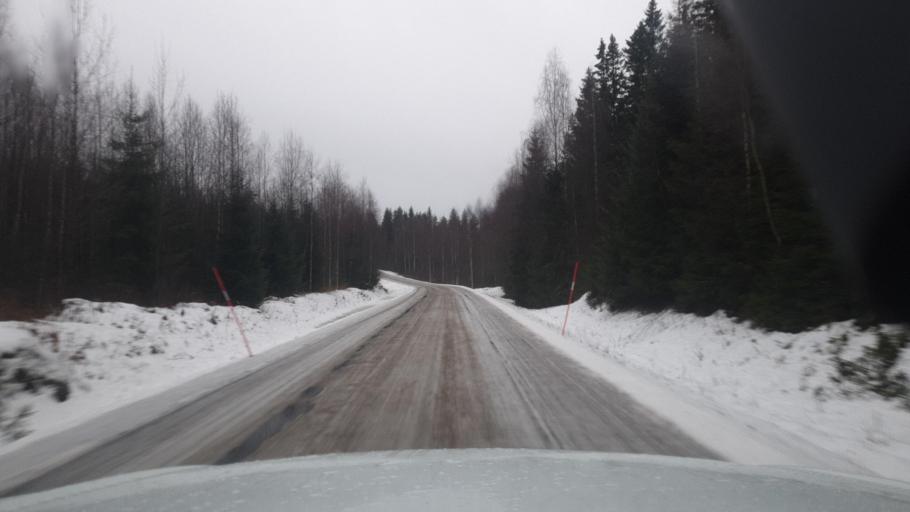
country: SE
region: Vaermland
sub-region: Torsby Kommun
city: Torsby
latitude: 59.9943
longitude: 12.7406
